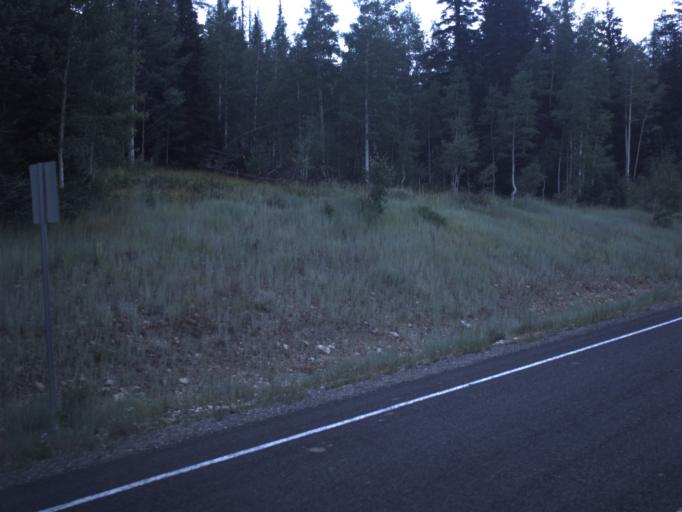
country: US
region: Utah
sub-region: Summit County
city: Francis
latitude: 40.4900
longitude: -110.9647
